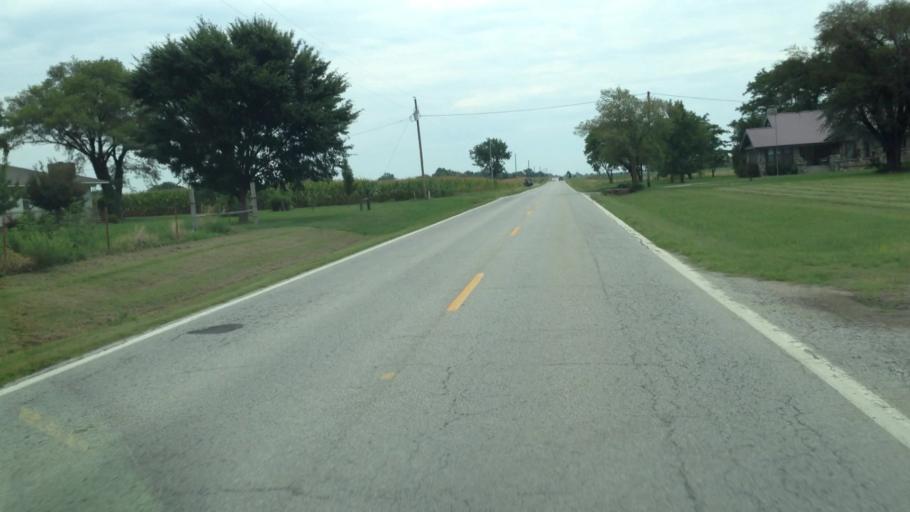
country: US
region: Oklahoma
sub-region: Delaware County
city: Cleora
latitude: 36.6191
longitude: -94.9815
